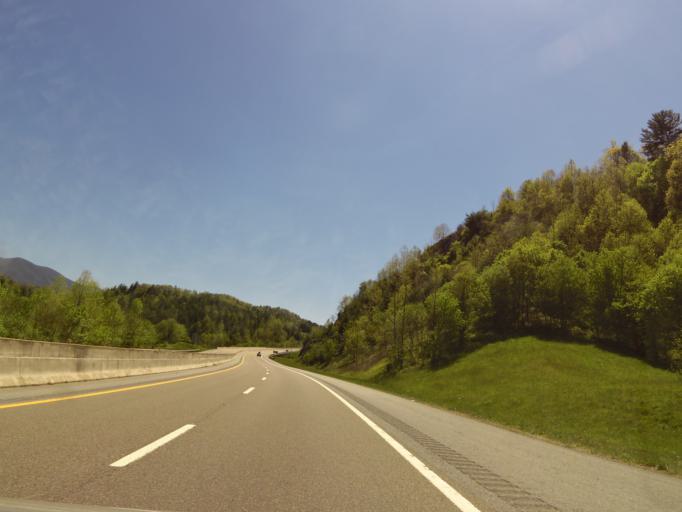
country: US
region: Tennessee
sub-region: Unicoi County
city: Banner Hill
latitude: 36.0733
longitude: -82.5031
